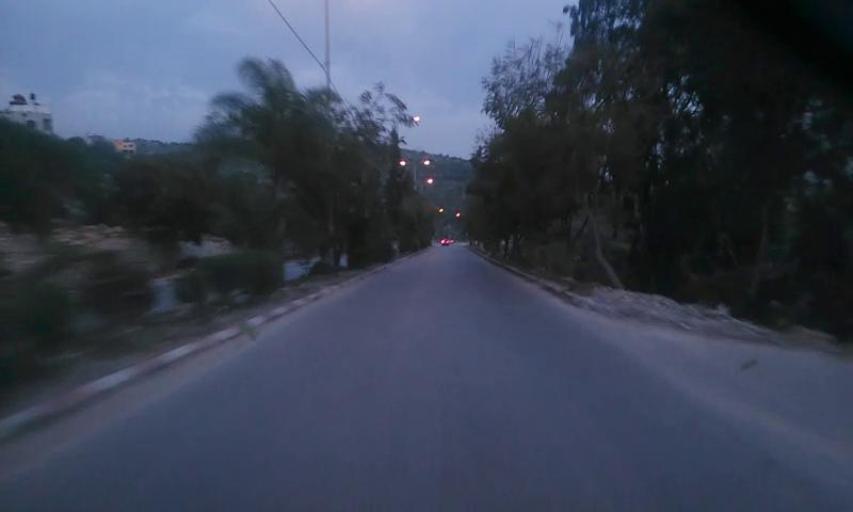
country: PS
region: West Bank
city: `Anabta
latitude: 32.3030
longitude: 35.1290
